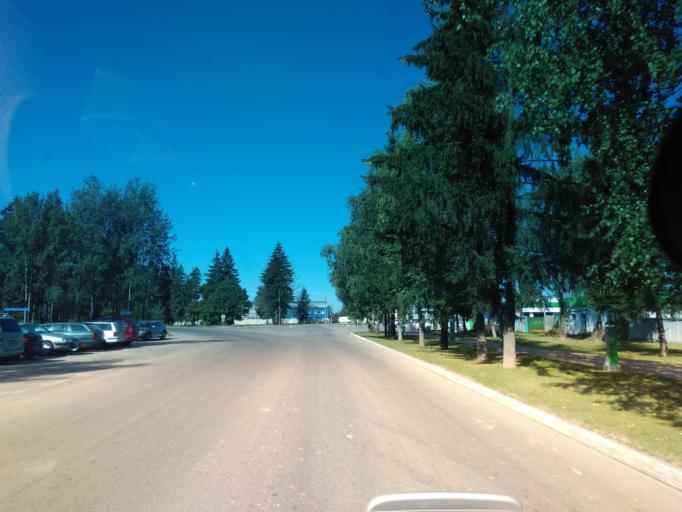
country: BY
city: Fanipol
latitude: 53.7411
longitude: 27.3463
